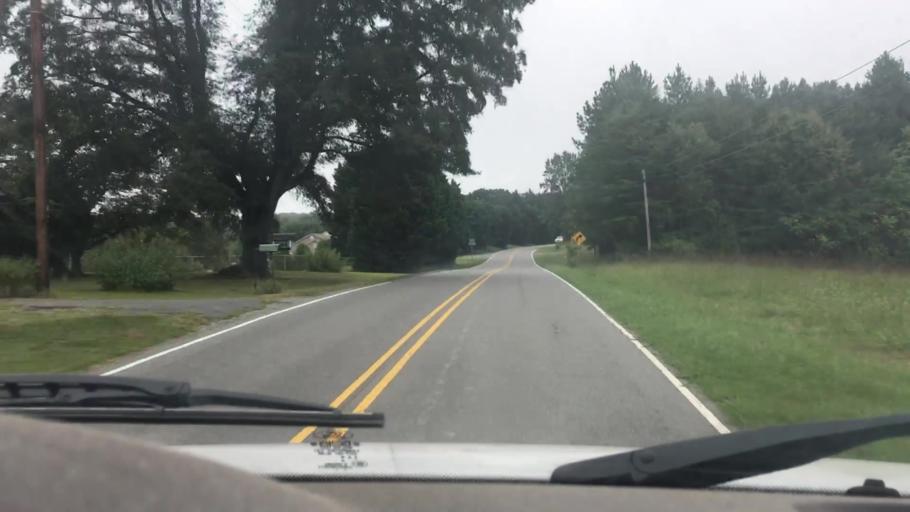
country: US
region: North Carolina
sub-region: Gaston County
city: Davidson
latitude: 35.4670
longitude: -80.7567
